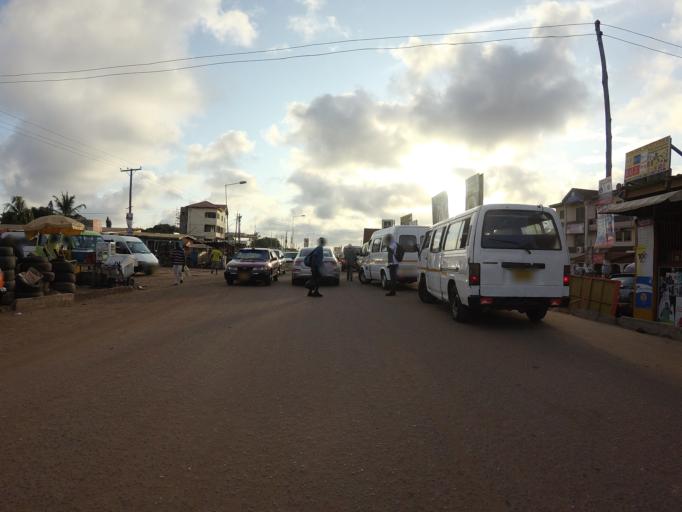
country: GH
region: Greater Accra
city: Teshi Old Town
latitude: 5.6061
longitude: -0.1156
